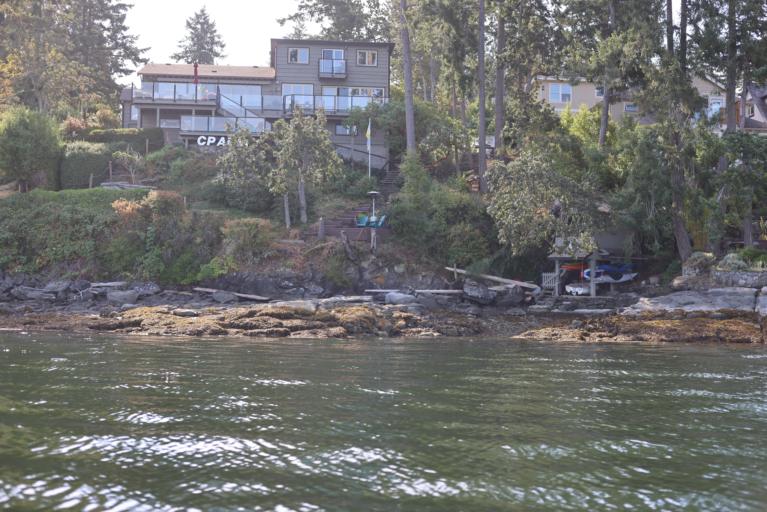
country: CA
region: British Columbia
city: North Saanich
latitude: 48.6800
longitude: -123.4831
